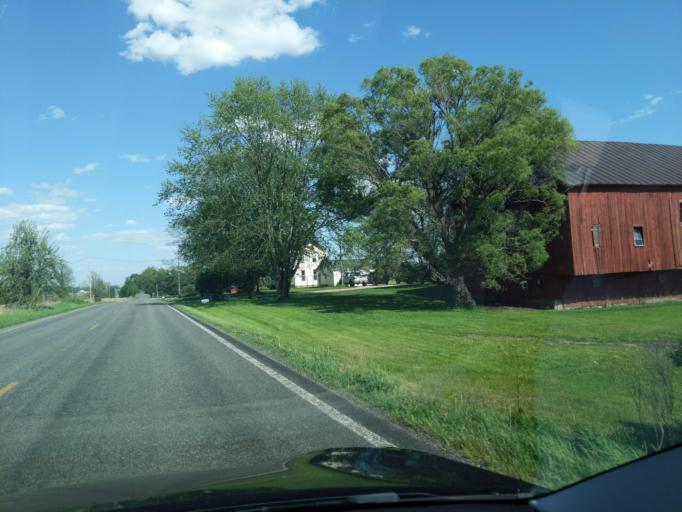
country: US
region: Michigan
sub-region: Ionia County
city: Lake Odessa
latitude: 42.7841
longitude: -85.2256
